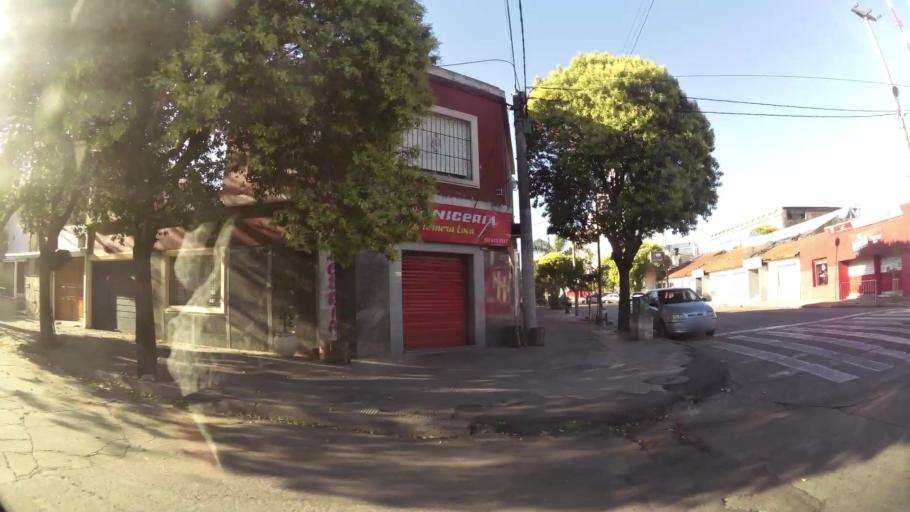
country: AR
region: Cordoba
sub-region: Departamento de Capital
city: Cordoba
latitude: -31.3852
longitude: -64.1812
